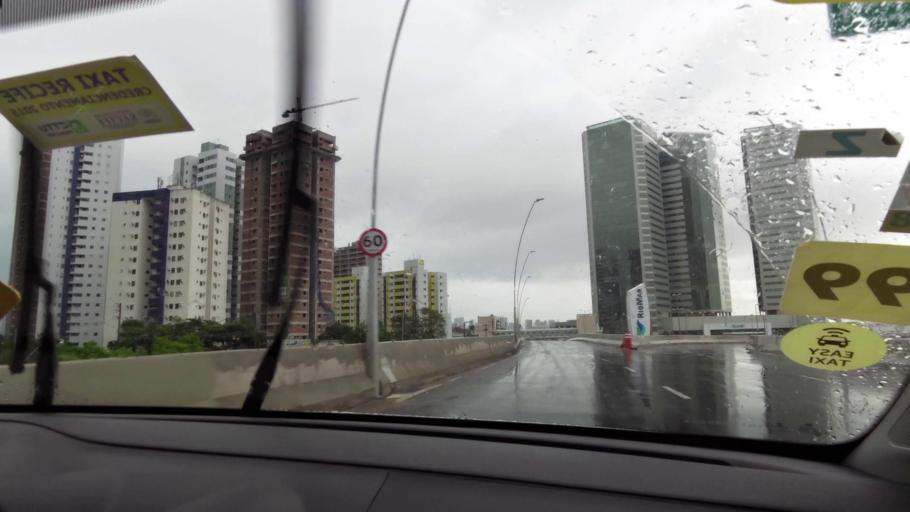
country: BR
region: Pernambuco
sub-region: Recife
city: Recife
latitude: -8.1153
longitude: -34.9007
